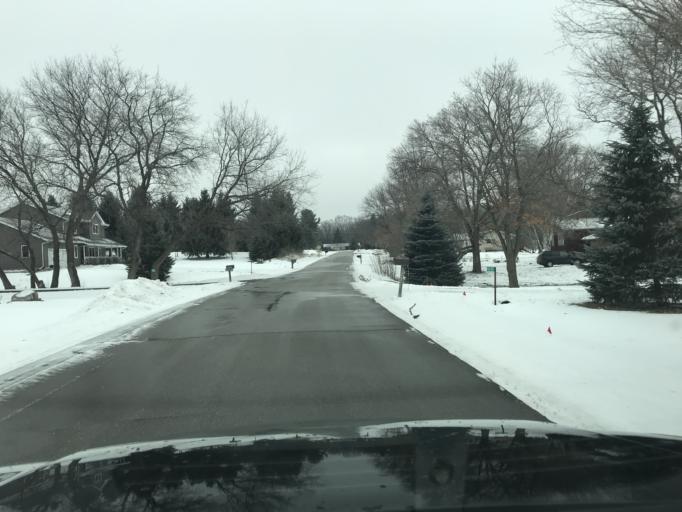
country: US
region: Wisconsin
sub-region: Dane County
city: Cottage Grove
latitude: 43.1025
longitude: -89.2183
